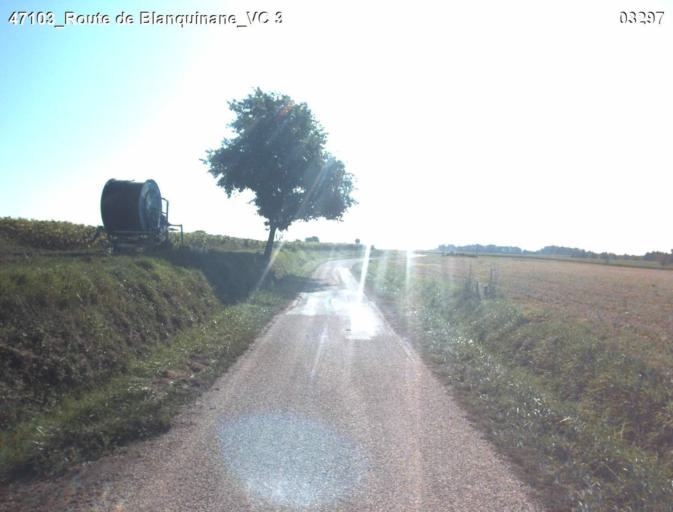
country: FR
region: Aquitaine
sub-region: Departement du Lot-et-Garonne
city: Nerac
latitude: 44.0901
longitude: 0.3270
